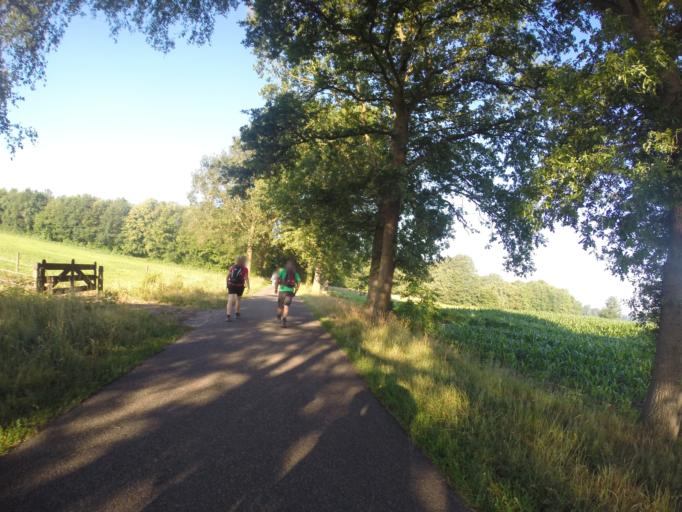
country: NL
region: Gelderland
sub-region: Gemeente Lochem
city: Barchem
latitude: 52.1022
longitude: 6.4247
